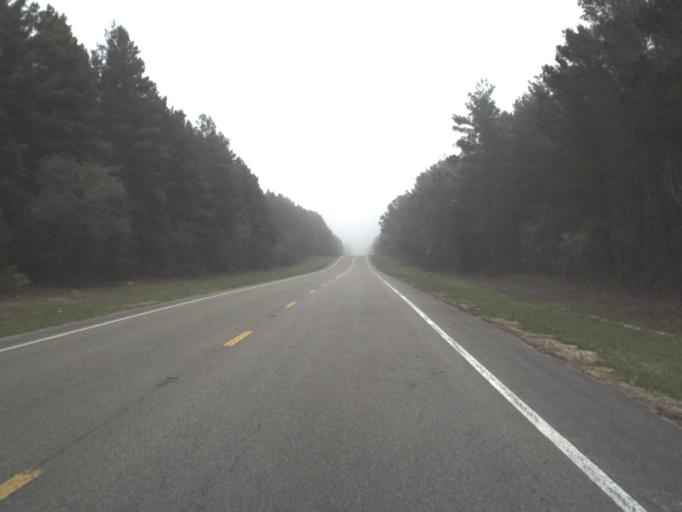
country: US
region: Florida
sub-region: Gadsden County
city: Gretna
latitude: 30.4703
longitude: -84.7336
